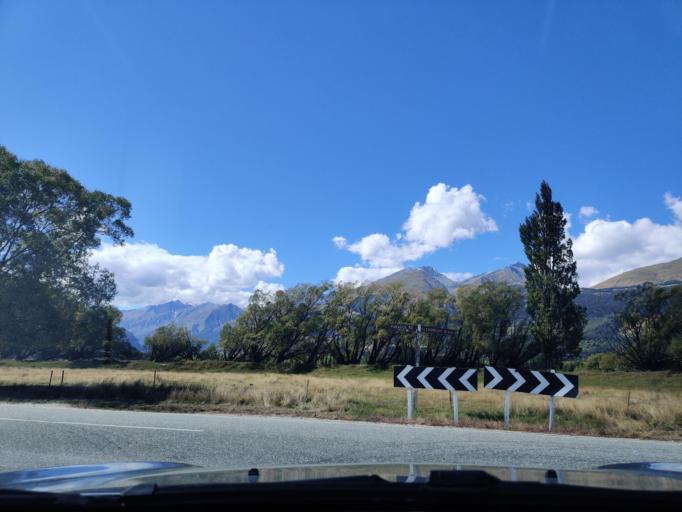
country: NZ
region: Otago
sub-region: Queenstown-Lakes District
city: Queenstown
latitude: -44.7830
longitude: 168.3944
